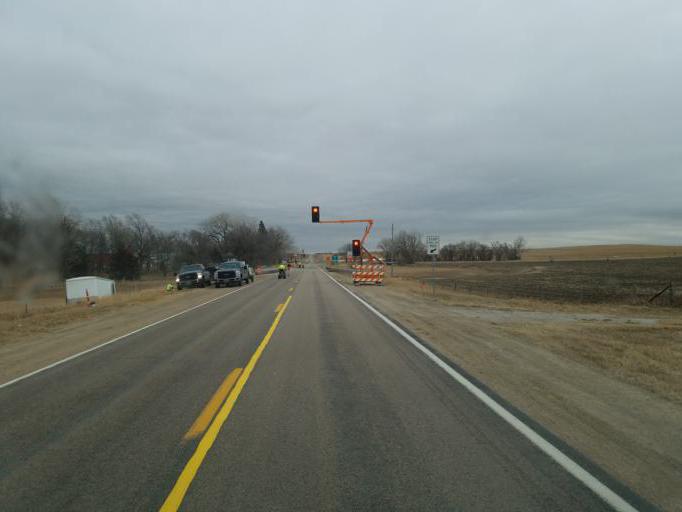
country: US
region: Nebraska
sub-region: Cedar County
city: Hartington
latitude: 42.6128
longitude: -97.4319
